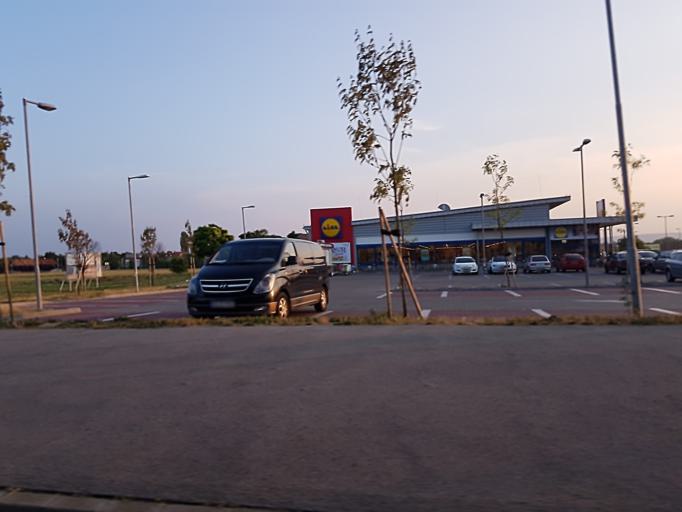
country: HU
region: Budapest
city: Budapest XVI. keruelet
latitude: 47.5346
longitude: 19.1610
